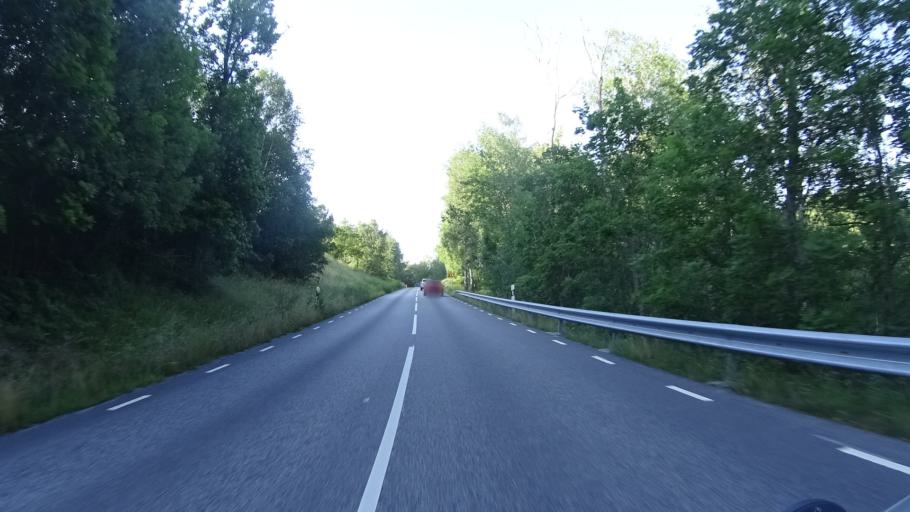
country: SE
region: Stockholm
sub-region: Sodertalje Kommun
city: Pershagen
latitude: 59.1031
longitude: 17.6334
